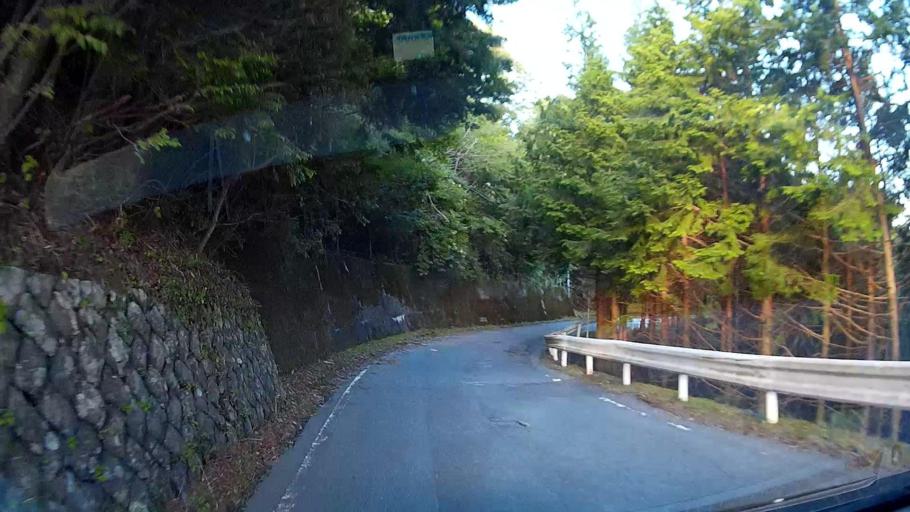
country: JP
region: Shizuoka
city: Shizuoka-shi
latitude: 35.1670
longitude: 138.2603
